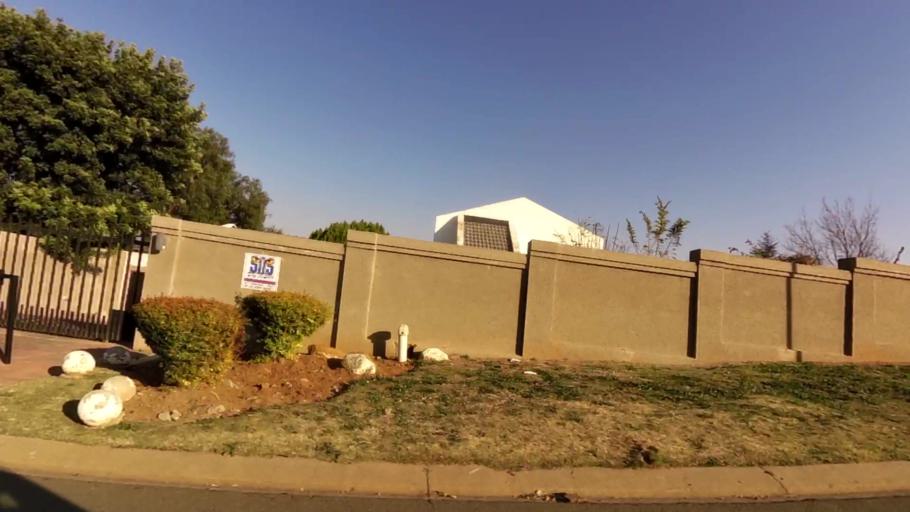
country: ZA
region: Gauteng
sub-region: City of Johannesburg Metropolitan Municipality
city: Soweto
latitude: -26.2904
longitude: 27.9551
